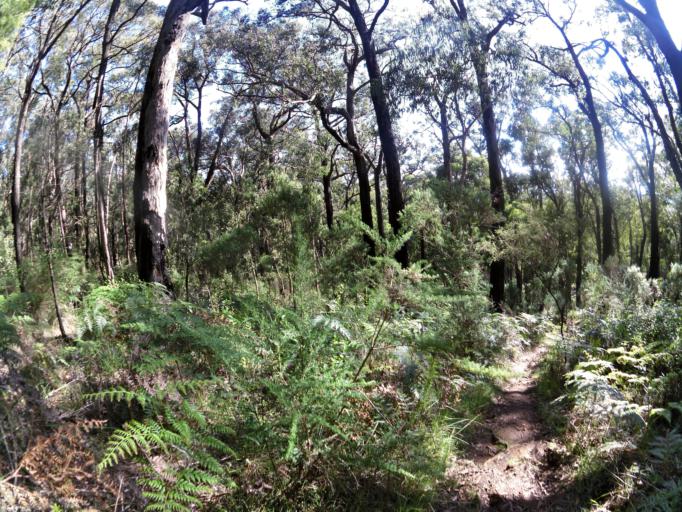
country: AU
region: Victoria
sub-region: Yarra Ranges
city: Ferny Creek
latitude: -37.8718
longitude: 145.3168
